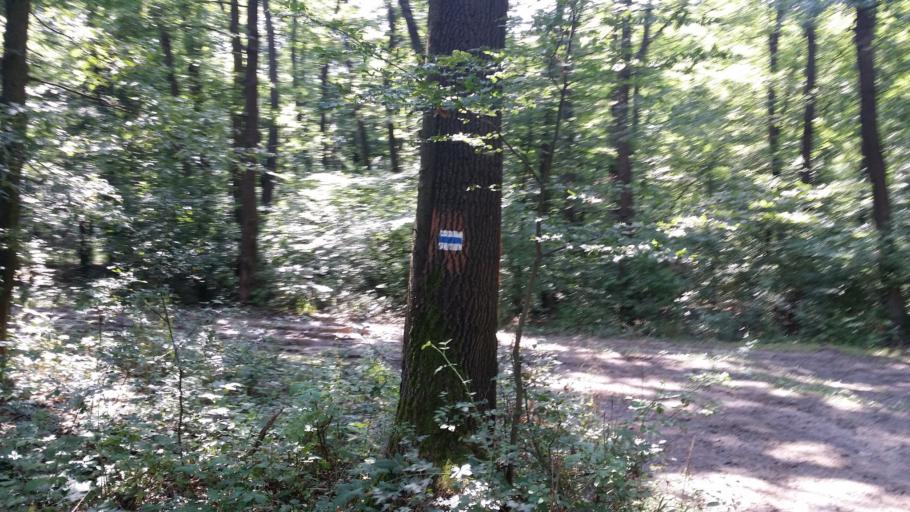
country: HU
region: Pest
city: Nagymaros
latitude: 47.8236
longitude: 18.9396
